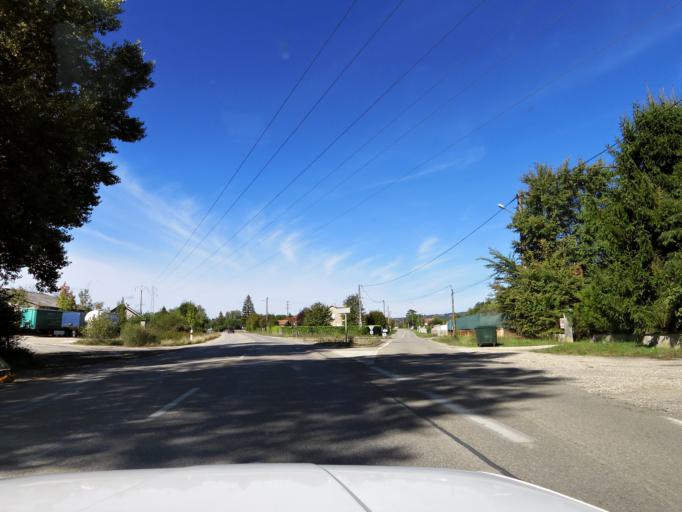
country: FR
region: Rhone-Alpes
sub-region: Departement de l'Isere
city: Bouvesse-Quirieu
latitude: 45.8056
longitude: 5.4119
